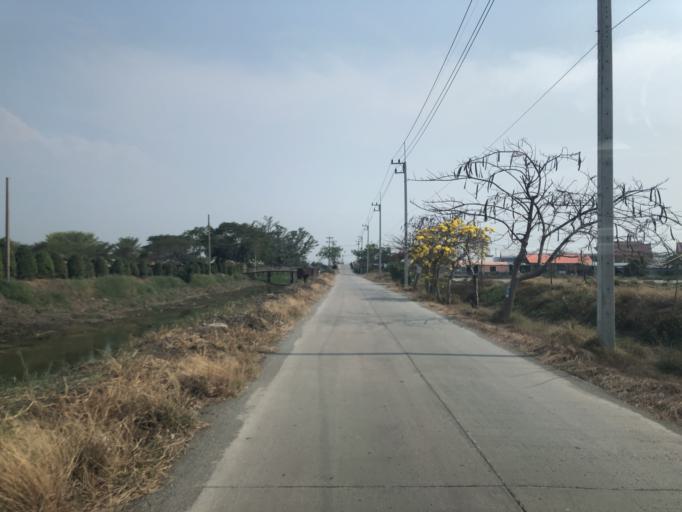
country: TH
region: Samut Prakan
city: Bang Bo
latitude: 13.5338
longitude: 100.9035
